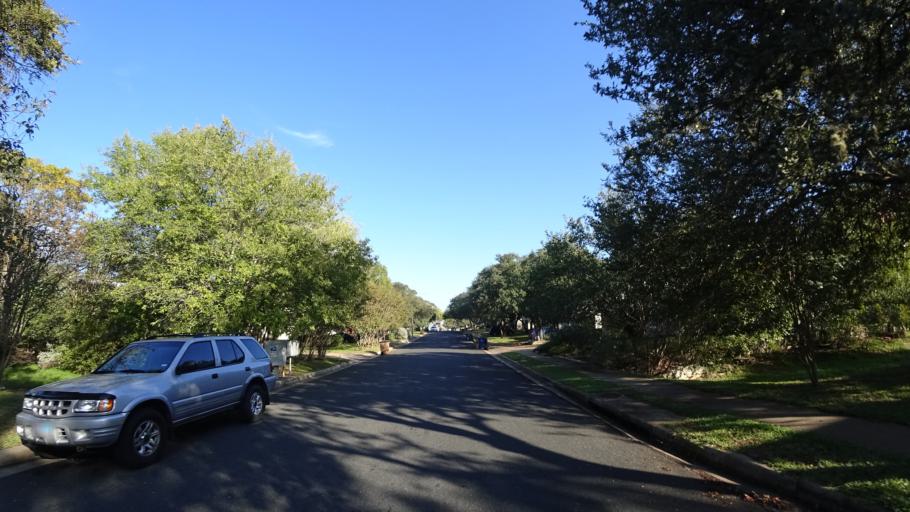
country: US
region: Texas
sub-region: Travis County
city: Shady Hollow
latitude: 30.2102
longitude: -97.8483
